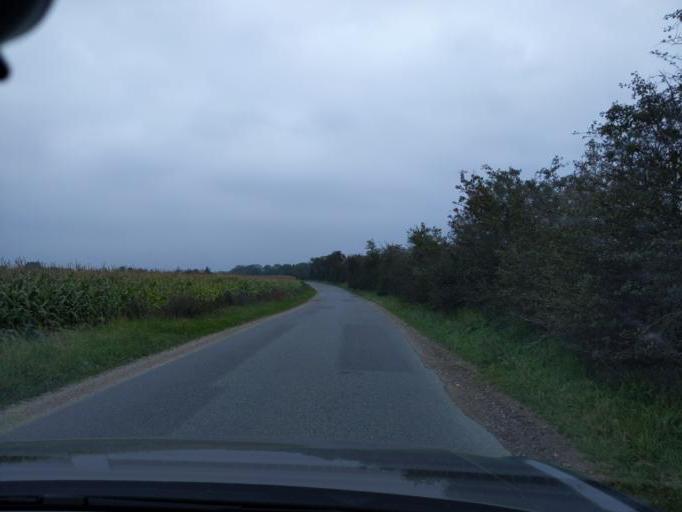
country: DK
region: Central Jutland
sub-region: Viborg Kommune
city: Stoholm
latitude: 56.5097
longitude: 9.2537
